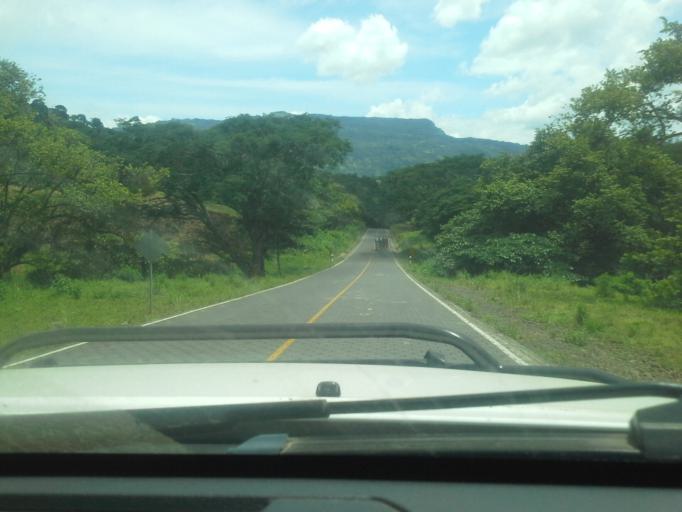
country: NI
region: Boaco
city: San Jose de los Remates
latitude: 12.6890
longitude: -85.7517
